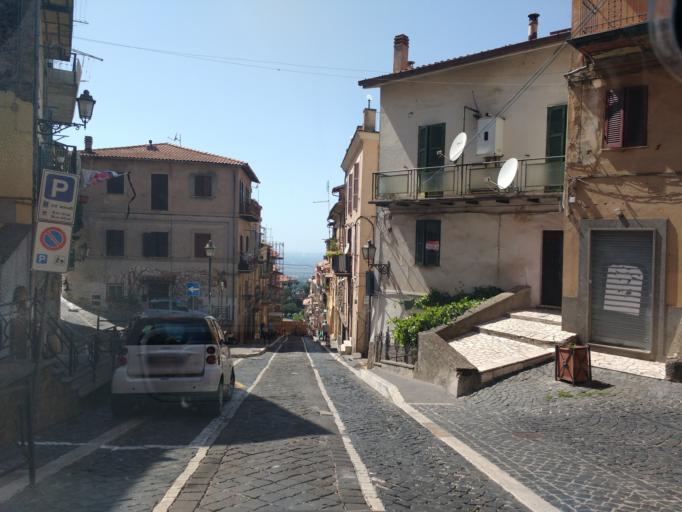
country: IT
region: Latium
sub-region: Citta metropolitana di Roma Capitale
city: Rocca di Papa
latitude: 41.7618
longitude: 12.7095
